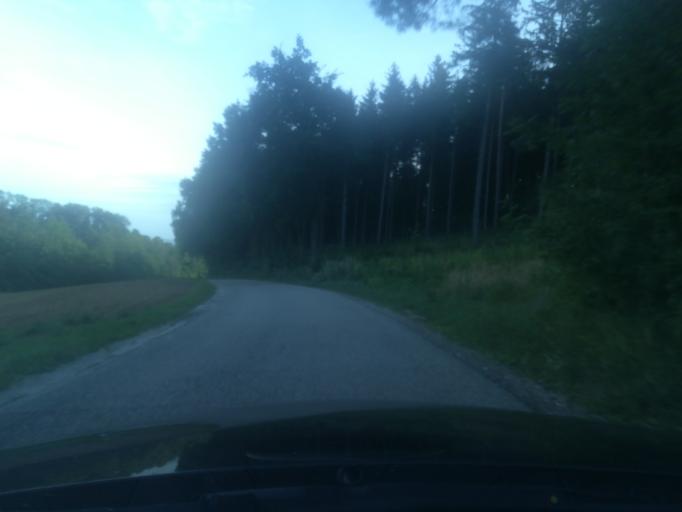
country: AT
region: Upper Austria
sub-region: Wels-Land
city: Marchtrenk
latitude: 48.1709
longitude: 14.1647
